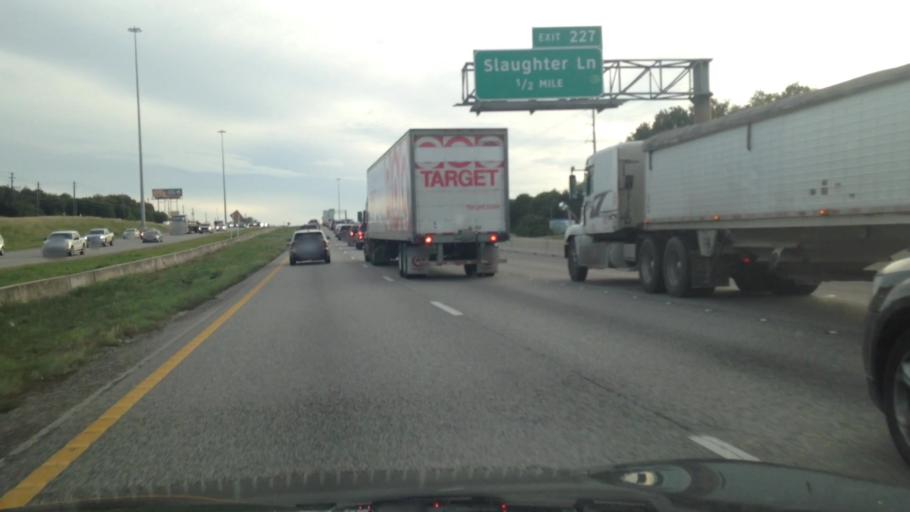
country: US
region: Texas
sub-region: Travis County
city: Onion Creek
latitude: 30.1791
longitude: -97.7783
